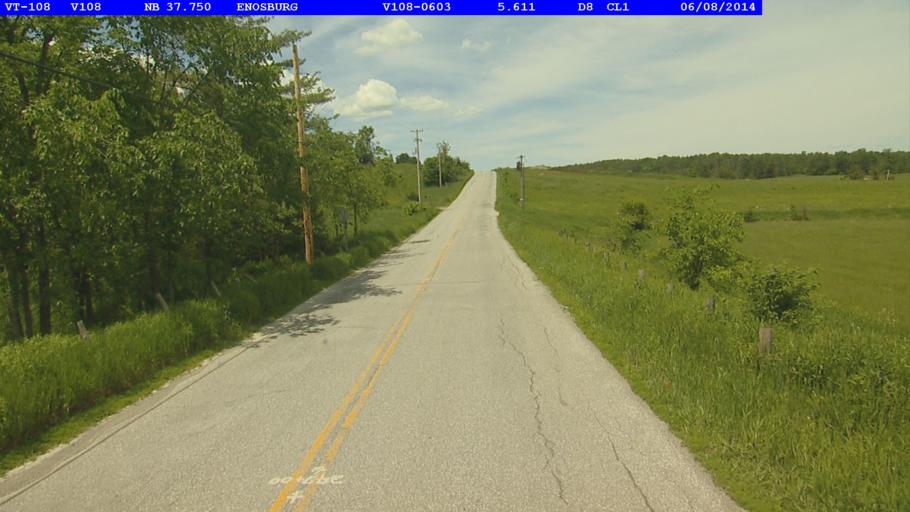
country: US
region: Vermont
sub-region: Franklin County
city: Enosburg Falls
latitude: 44.9210
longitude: -72.8076
